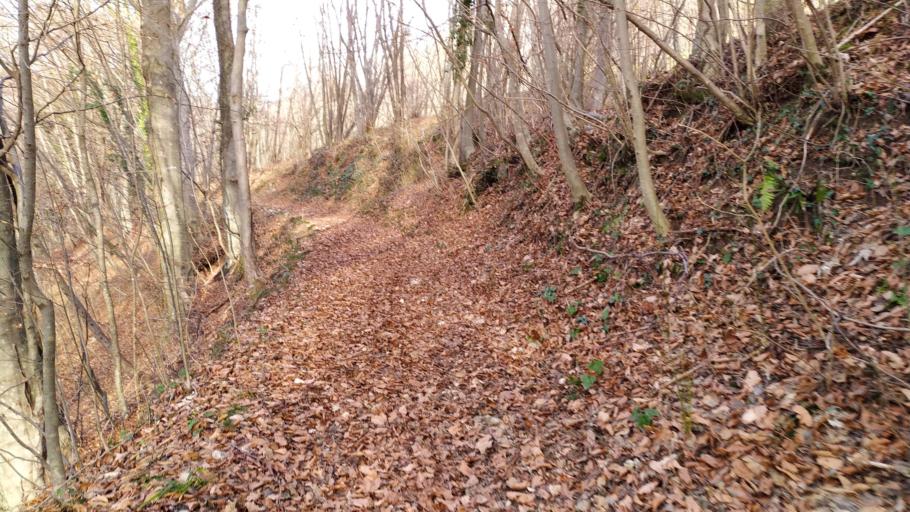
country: IT
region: Veneto
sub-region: Provincia di Vicenza
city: Velo d'Astico
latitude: 45.7611
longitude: 11.3584
